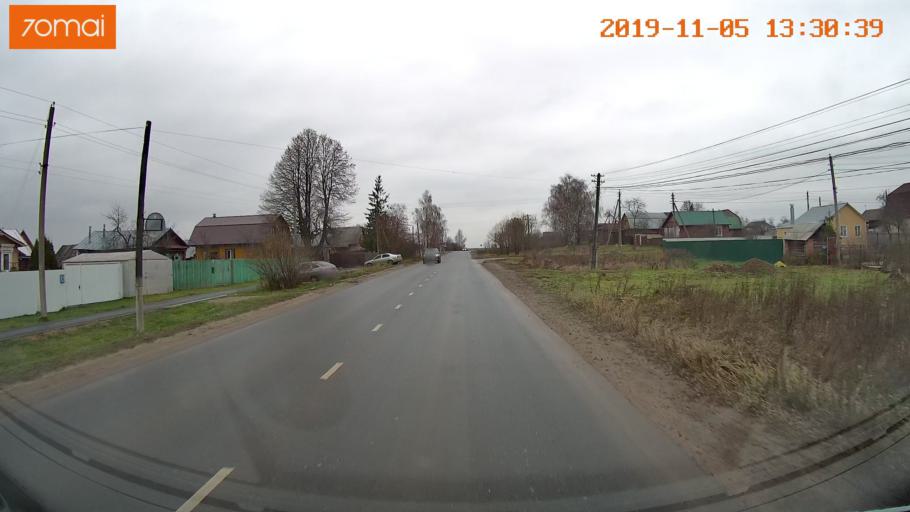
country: RU
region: Ivanovo
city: Shuya
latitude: 56.8686
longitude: 41.3948
